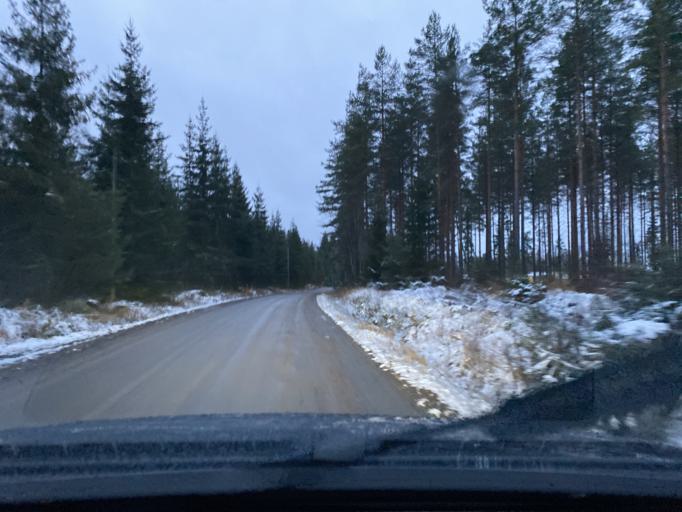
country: FI
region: Pirkanmaa
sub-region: Lounais-Pirkanmaa
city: Punkalaidun
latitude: 61.1485
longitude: 22.9497
